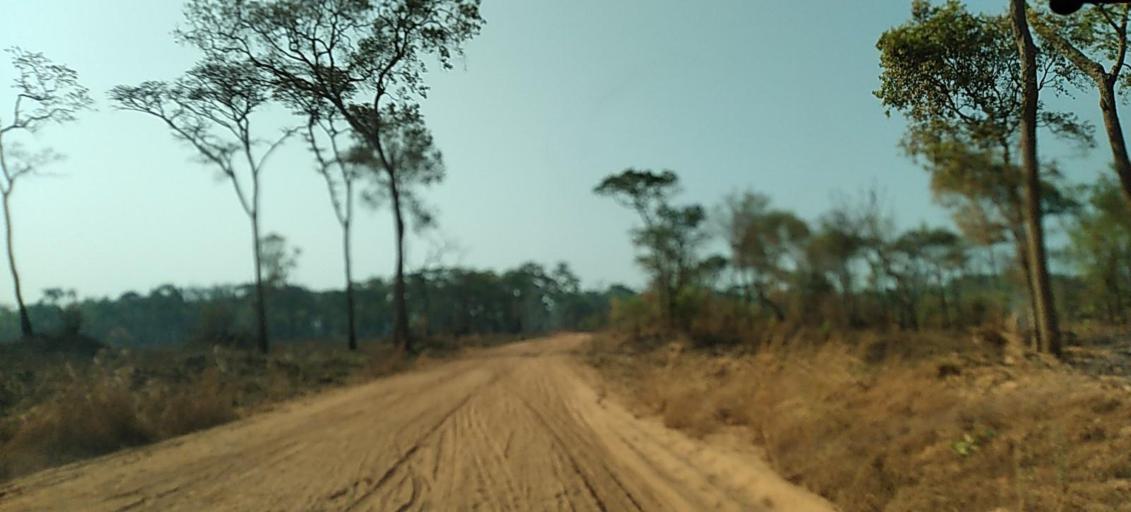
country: ZM
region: North-Western
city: Kasempa
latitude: -13.6243
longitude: 25.9830
